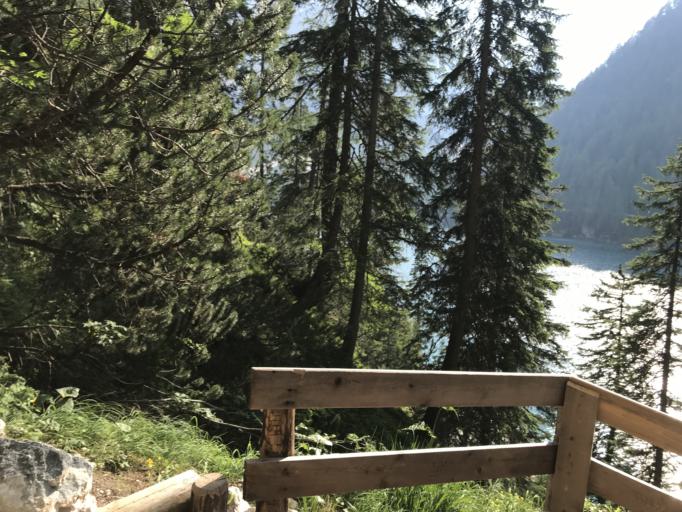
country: IT
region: Trentino-Alto Adige
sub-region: Bolzano
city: Braies
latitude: 46.6938
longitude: 12.0884
